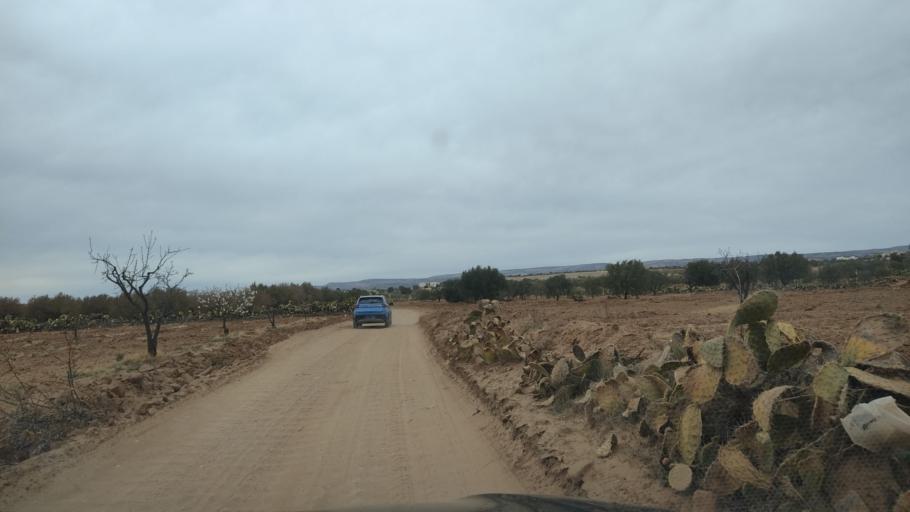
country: TN
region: Al Qasrayn
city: Kasserine
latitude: 35.2266
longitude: 8.9189
